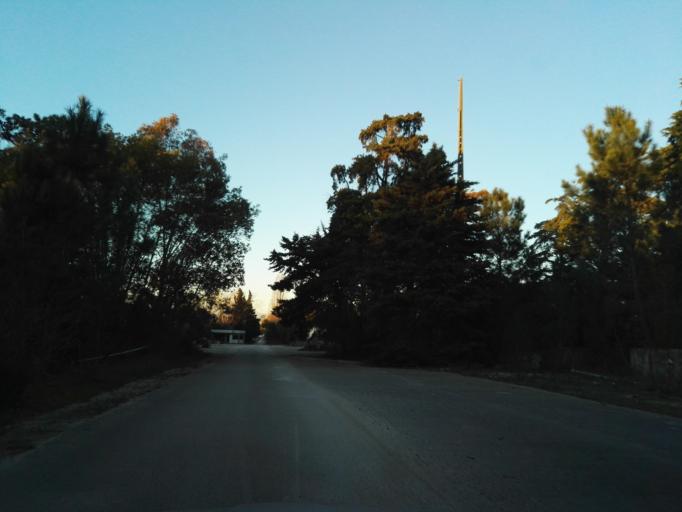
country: PT
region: Setubal
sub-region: Seixal
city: Corroios
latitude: 38.6207
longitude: -9.1461
